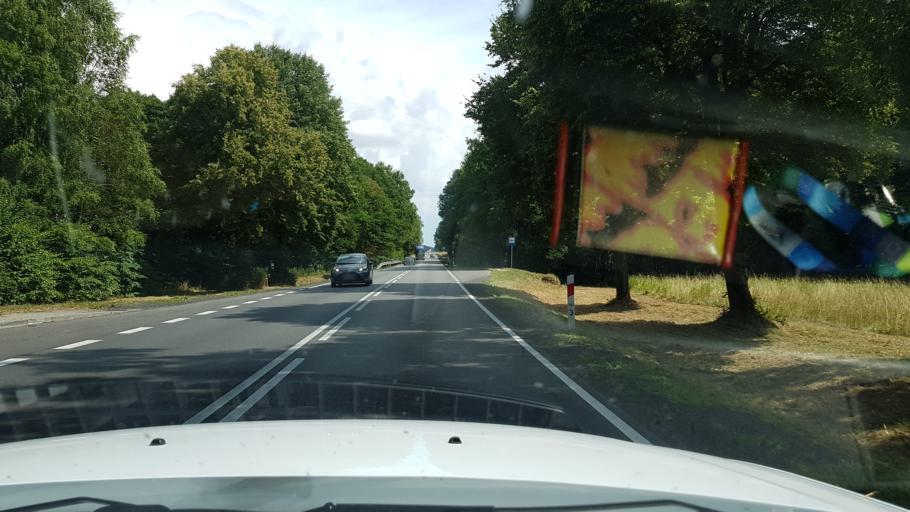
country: PL
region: West Pomeranian Voivodeship
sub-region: Powiat walecki
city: Walcz
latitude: 53.3045
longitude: 16.4048
